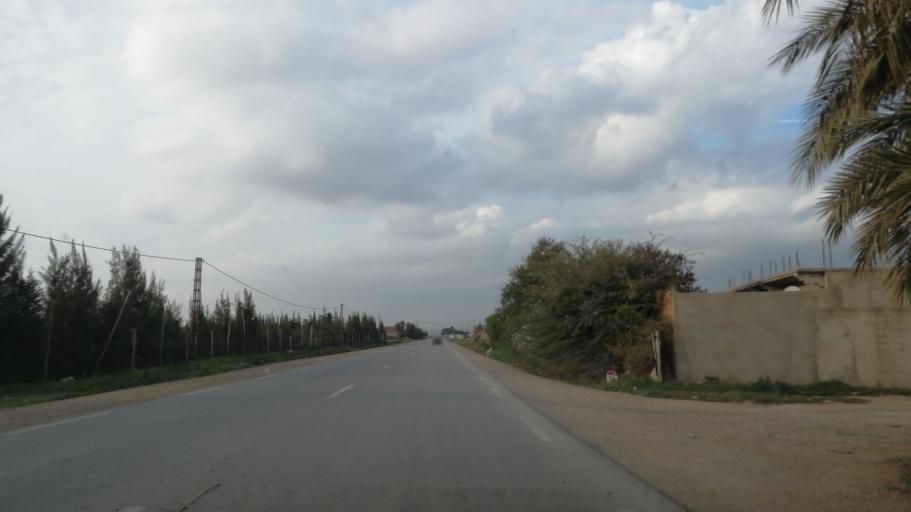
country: DZ
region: Mascara
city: Sig
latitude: 35.6877
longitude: -0.0156
